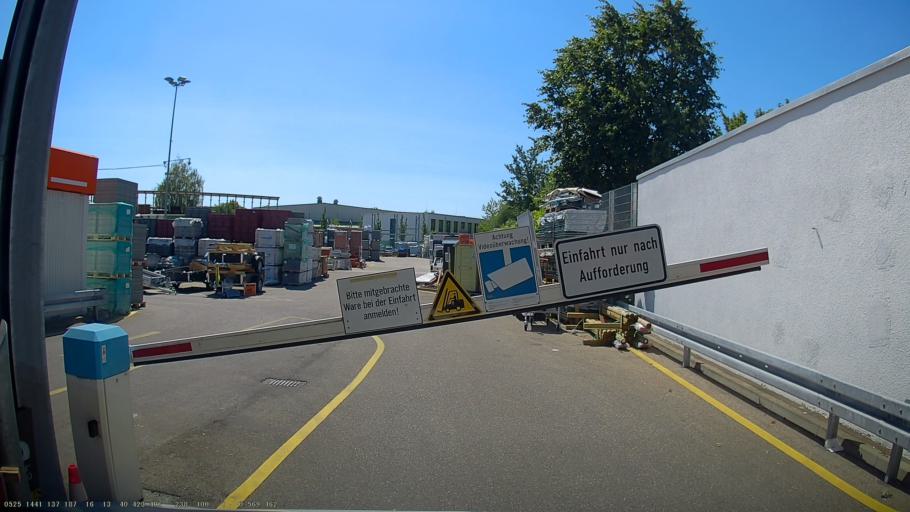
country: DE
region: Bavaria
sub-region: Swabia
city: Neu-Ulm
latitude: 48.3920
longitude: 10.0184
